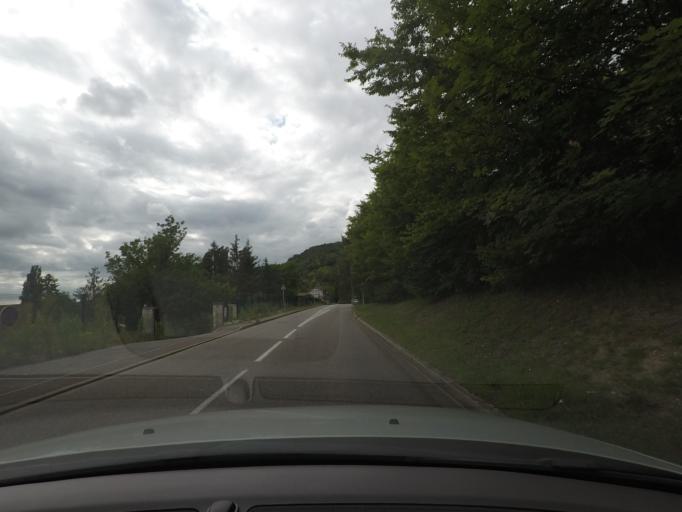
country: FR
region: Haute-Normandie
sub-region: Departement de l'Eure
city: Les Andelys
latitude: 49.2519
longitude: 1.3824
